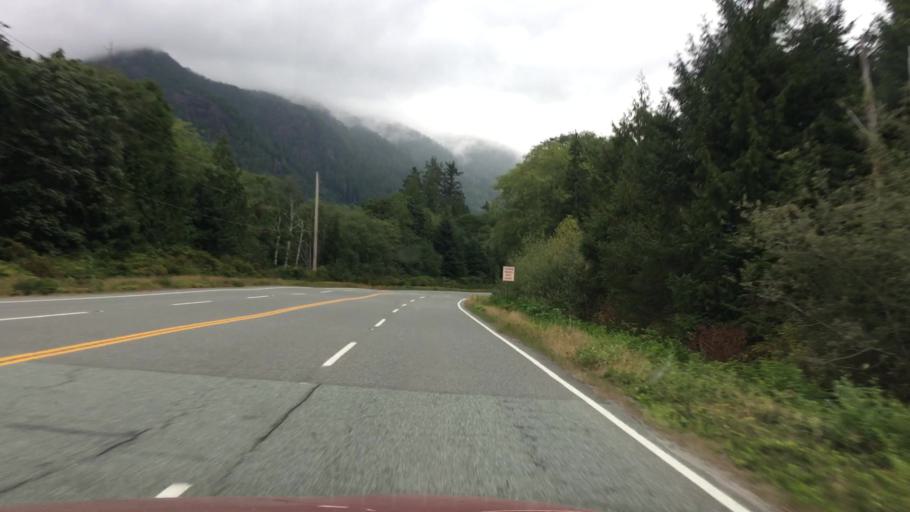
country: CA
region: British Columbia
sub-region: Regional District of Alberni-Clayoquot
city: Ucluelet
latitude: 49.1374
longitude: -125.4178
